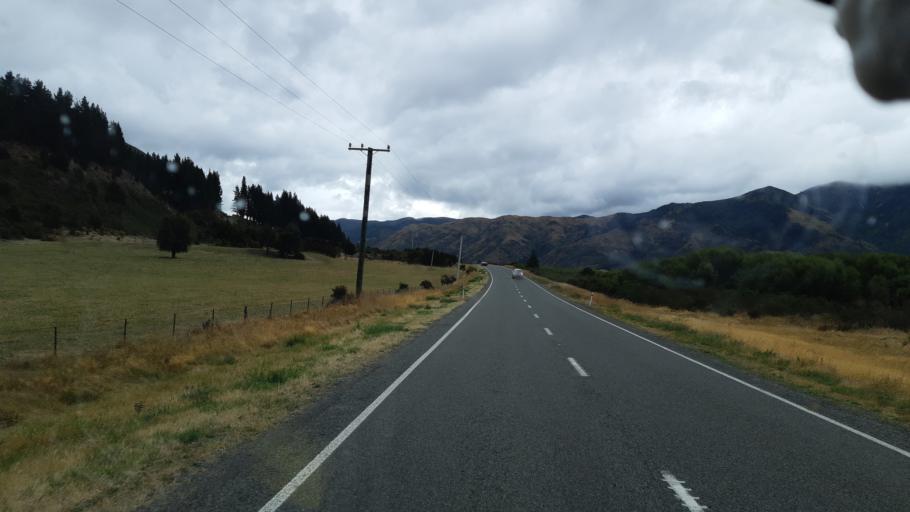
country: NZ
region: Canterbury
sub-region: Hurunui District
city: Amberley
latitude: -42.5705
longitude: 172.7026
